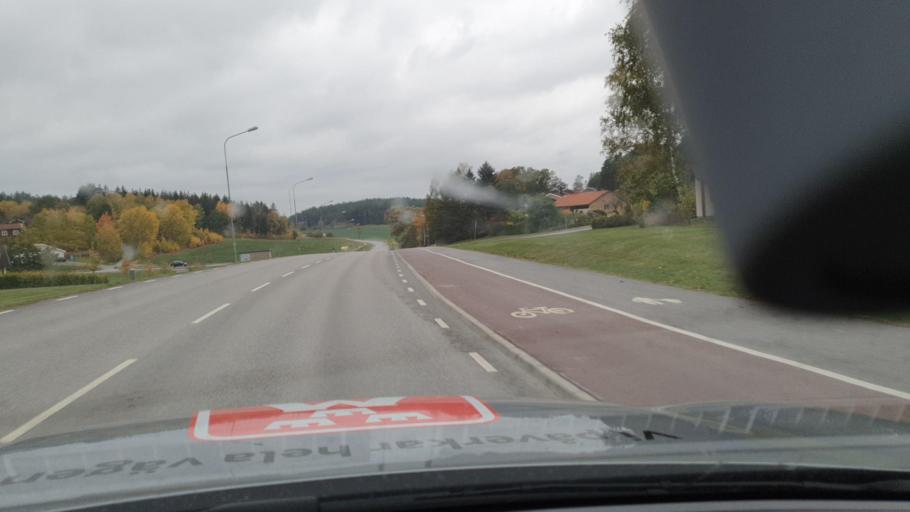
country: SE
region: OEstergoetland
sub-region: Soderkopings Kommun
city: Soederkoeping
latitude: 58.4712
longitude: 16.3123
